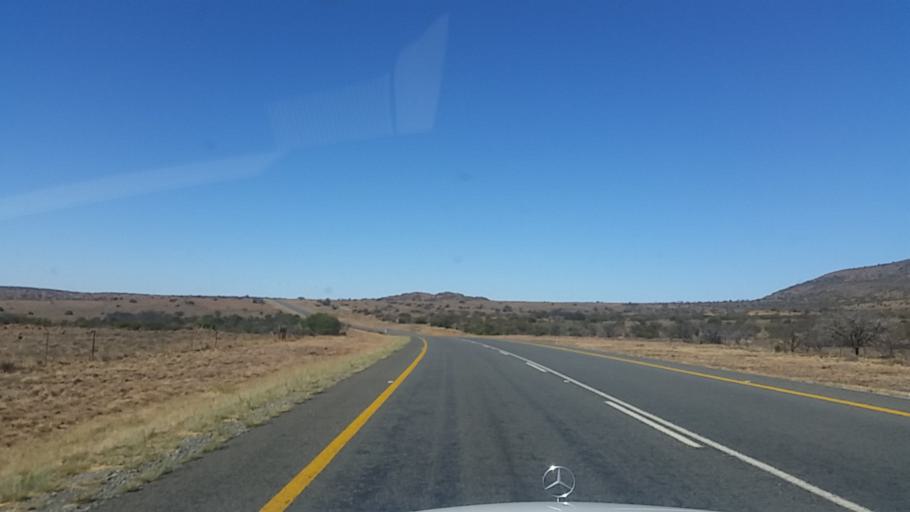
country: ZA
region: Eastern Cape
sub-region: Cacadu District Municipality
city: Graaff-Reinet
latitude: -32.0385
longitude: 24.6202
